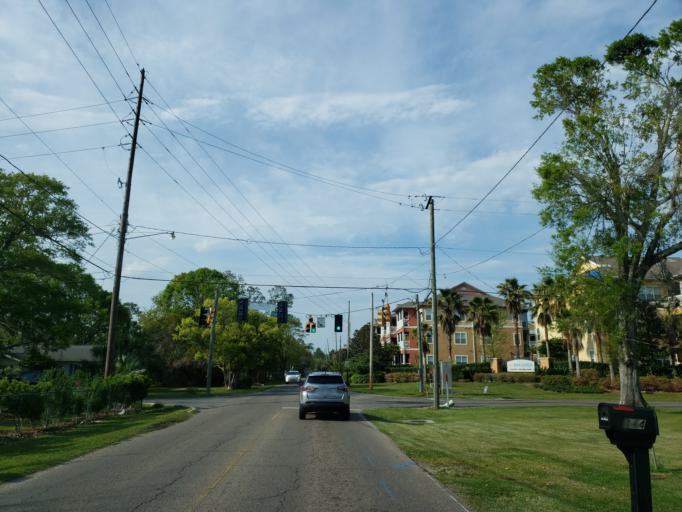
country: US
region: Mississippi
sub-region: Harrison County
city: West Gulfport
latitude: 30.3979
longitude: -89.0444
